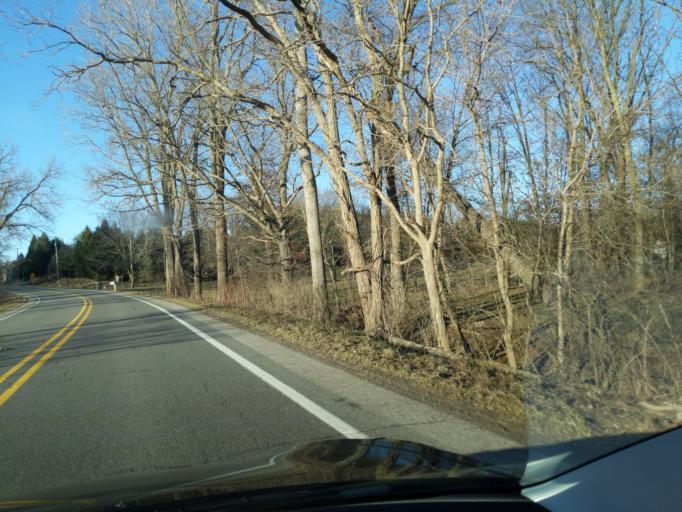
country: US
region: Michigan
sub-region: Washtenaw County
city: Chelsea
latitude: 42.3441
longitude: -84.0253
